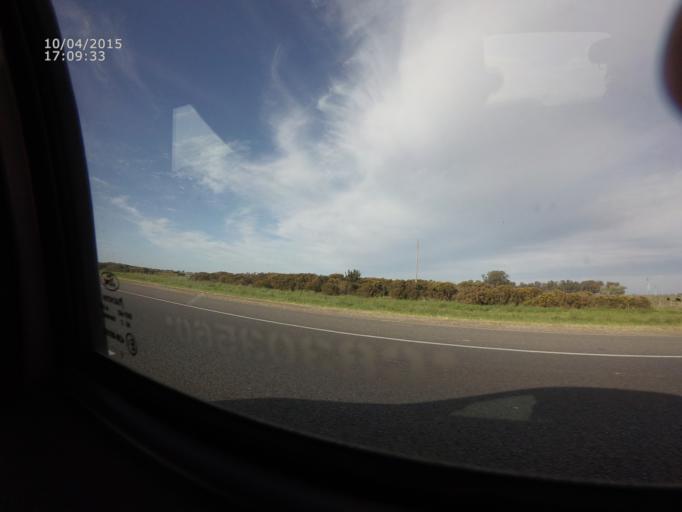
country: AR
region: Buenos Aires
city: Coronel Vidal
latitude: -37.3121
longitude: -57.7677
